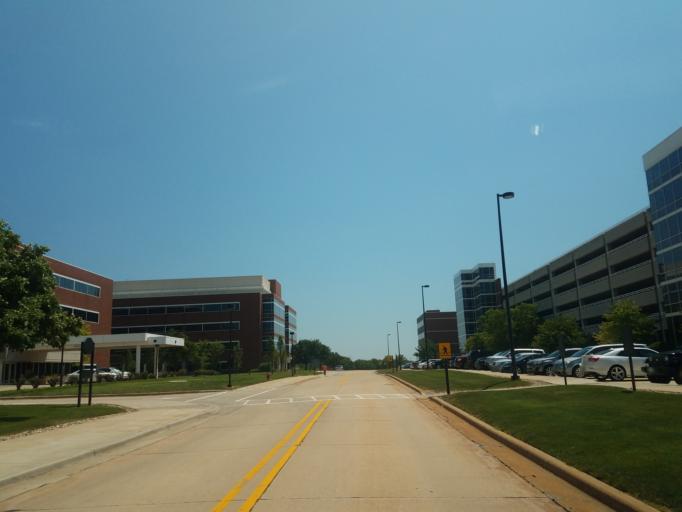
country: US
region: Illinois
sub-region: McLean County
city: Bloomington
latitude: 40.4552
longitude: -88.9554
